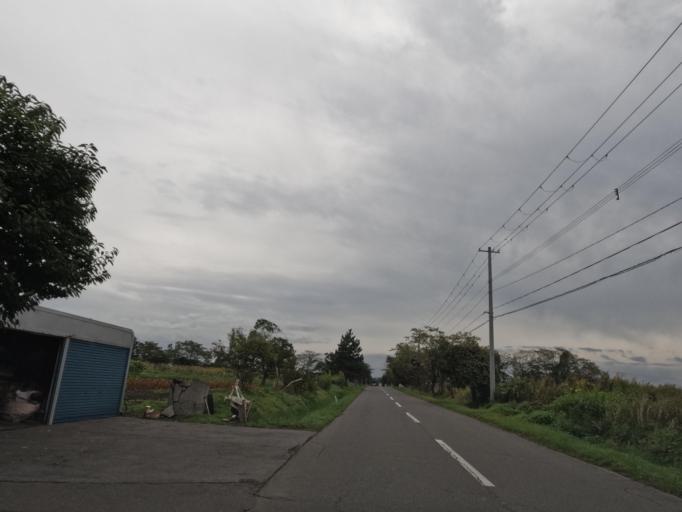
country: JP
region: Hokkaido
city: Date
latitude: 42.4337
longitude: 140.9090
